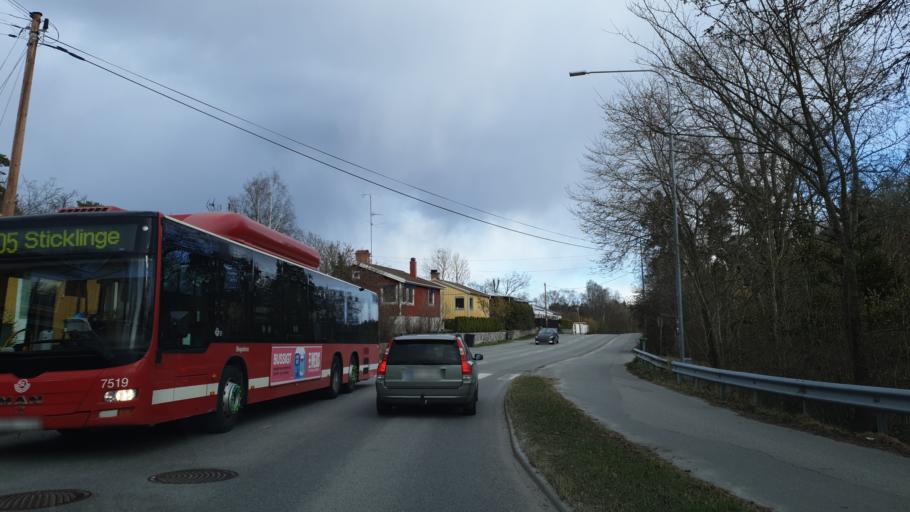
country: SE
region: Stockholm
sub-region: Lidingo
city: Lidingoe
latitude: 59.3752
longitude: 18.1296
